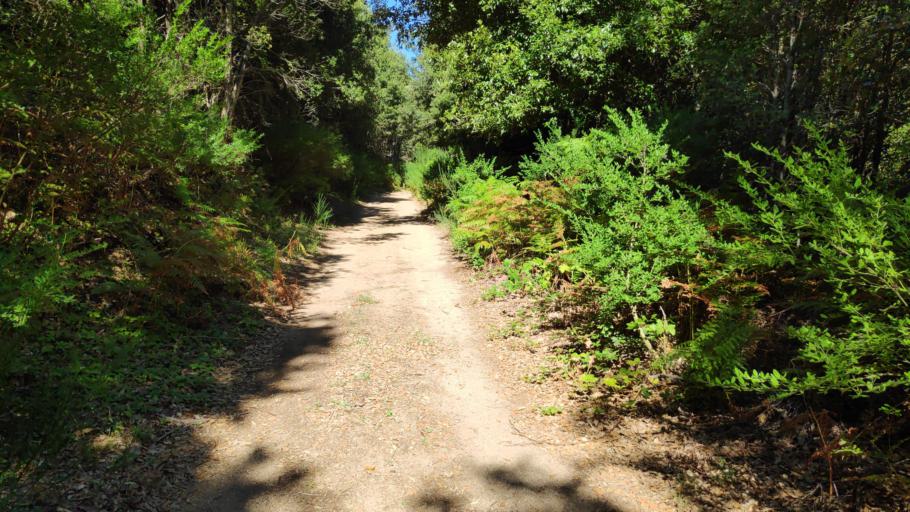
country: IT
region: Calabria
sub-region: Provincia di Vibo-Valentia
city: Nardodipace
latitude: 38.4788
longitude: 16.3896
